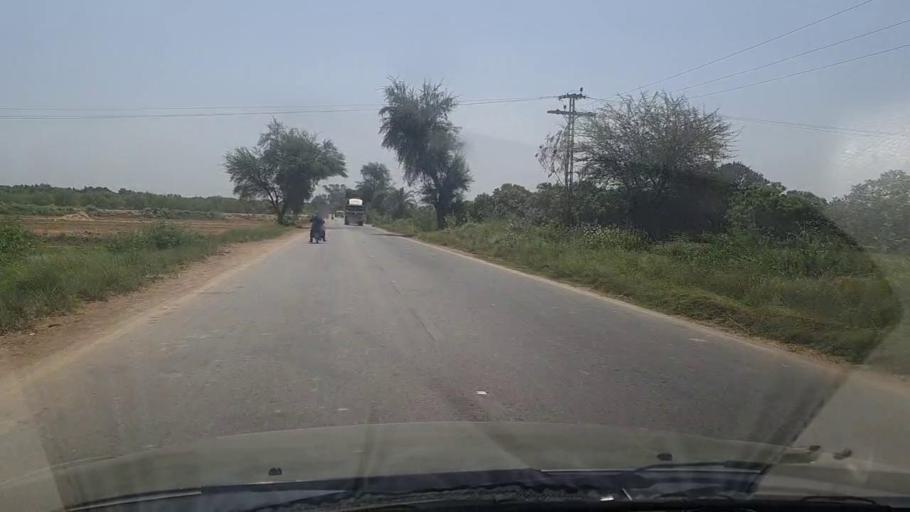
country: PK
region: Sindh
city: Tando Jam
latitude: 25.3548
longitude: 68.5024
